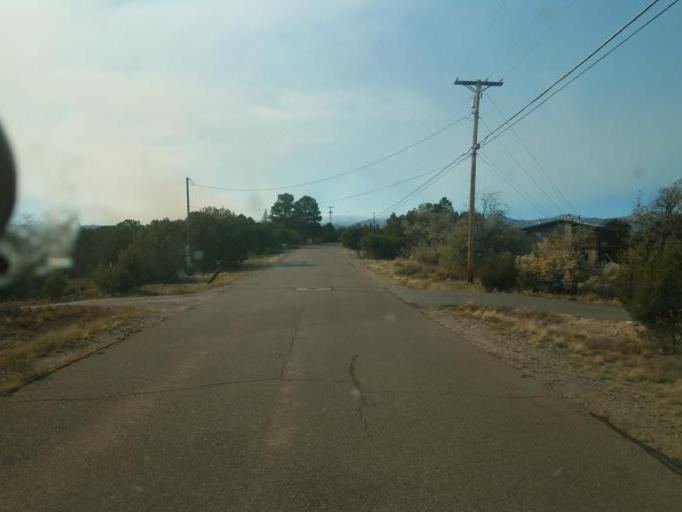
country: US
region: New Mexico
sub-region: Los Alamos County
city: White Rock
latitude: 35.8080
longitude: -106.2193
